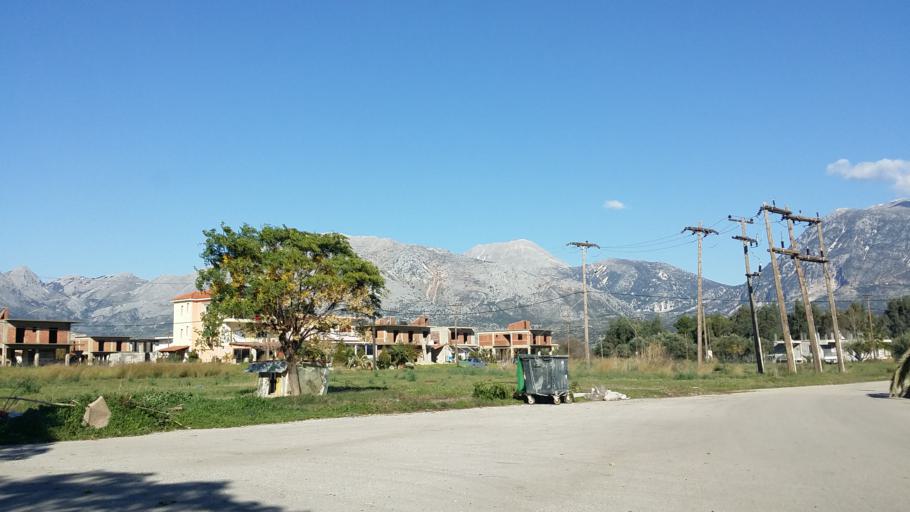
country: GR
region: West Greece
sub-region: Nomos Aitolias kai Akarnanias
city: Kandila
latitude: 38.6700
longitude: 20.9502
